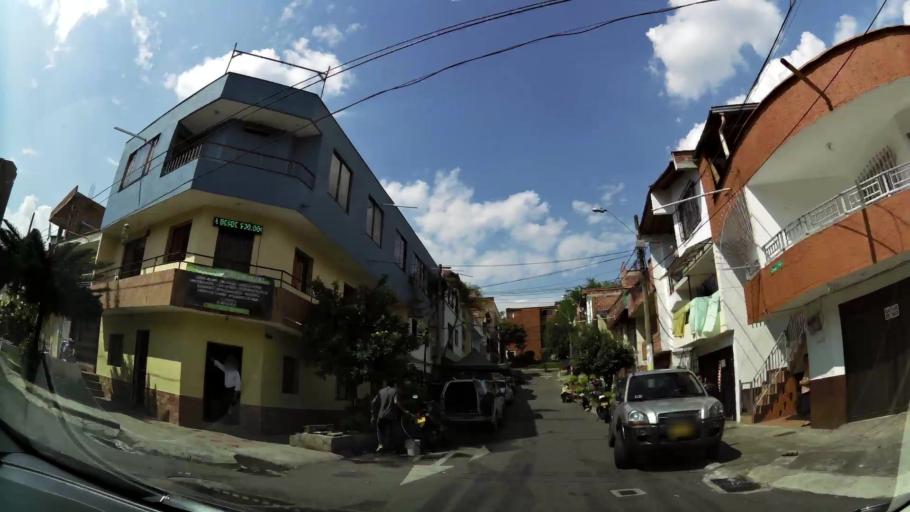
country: CO
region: Antioquia
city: Itagui
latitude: 6.2197
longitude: -75.5981
